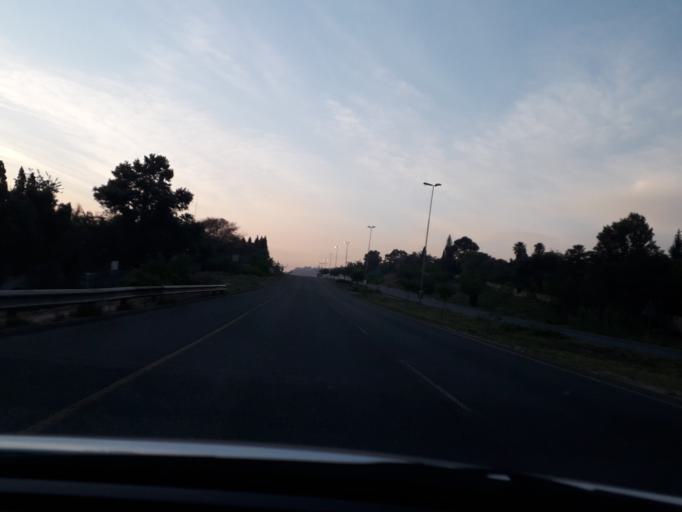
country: ZA
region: Gauteng
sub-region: City of Johannesburg Metropolitan Municipality
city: Roodepoort
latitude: -26.1055
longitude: 27.9477
